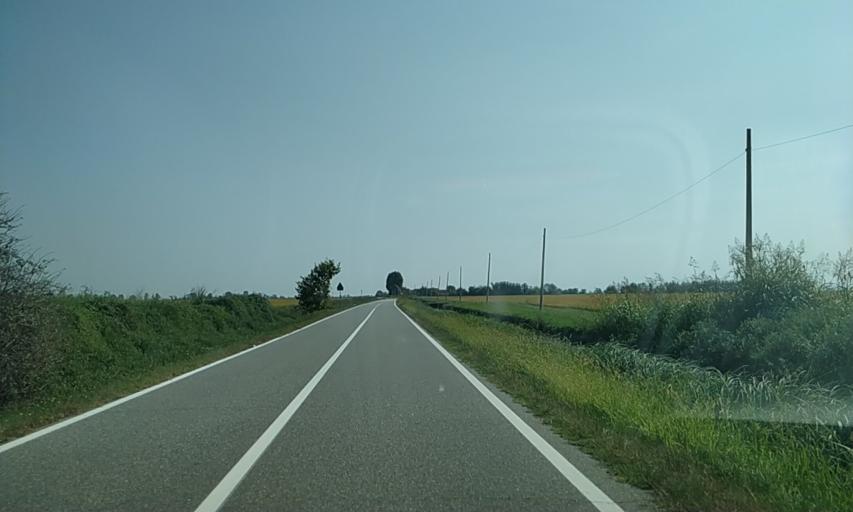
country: IT
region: Piedmont
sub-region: Provincia di Vercelli
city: Crova
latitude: 45.3190
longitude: 8.2268
